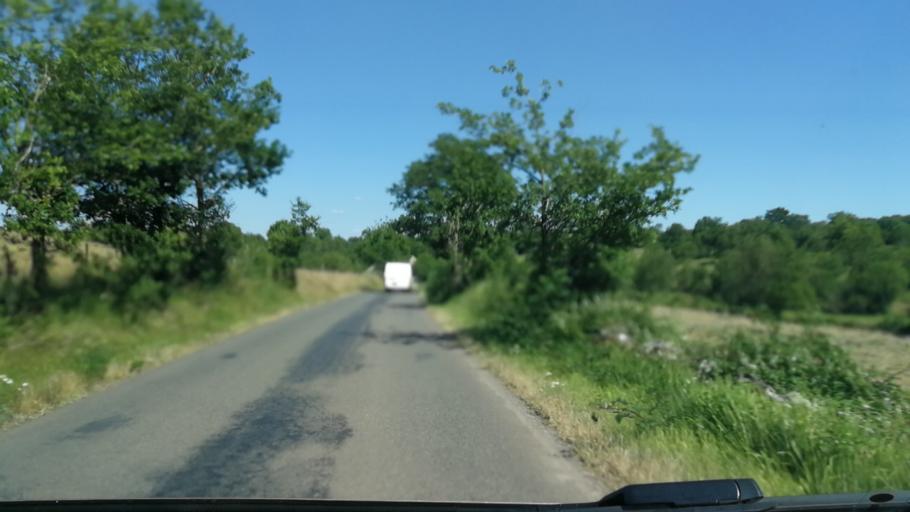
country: FR
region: Midi-Pyrenees
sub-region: Departement de l'Aveyron
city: Salles-la-Source
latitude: 44.4222
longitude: 2.5561
